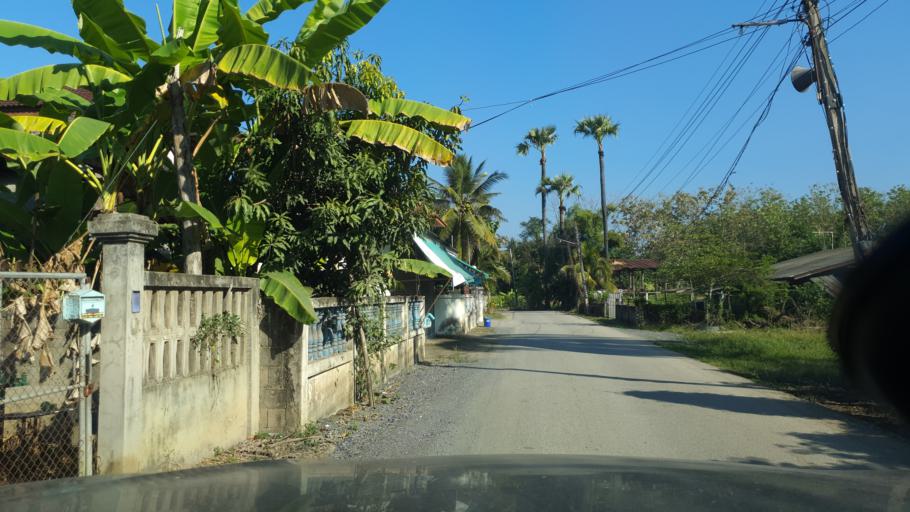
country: TH
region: Chiang Mai
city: San Kamphaeng
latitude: 18.7432
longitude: 99.1719
